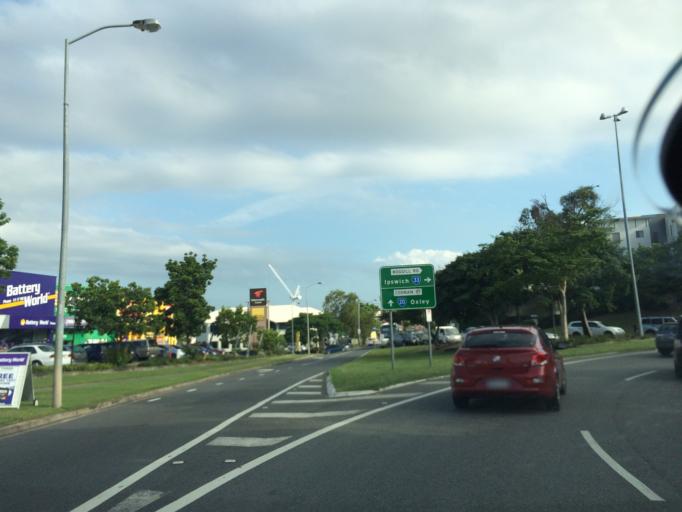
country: AU
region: Queensland
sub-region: Brisbane
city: Taringa
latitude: -27.4970
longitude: 152.9757
